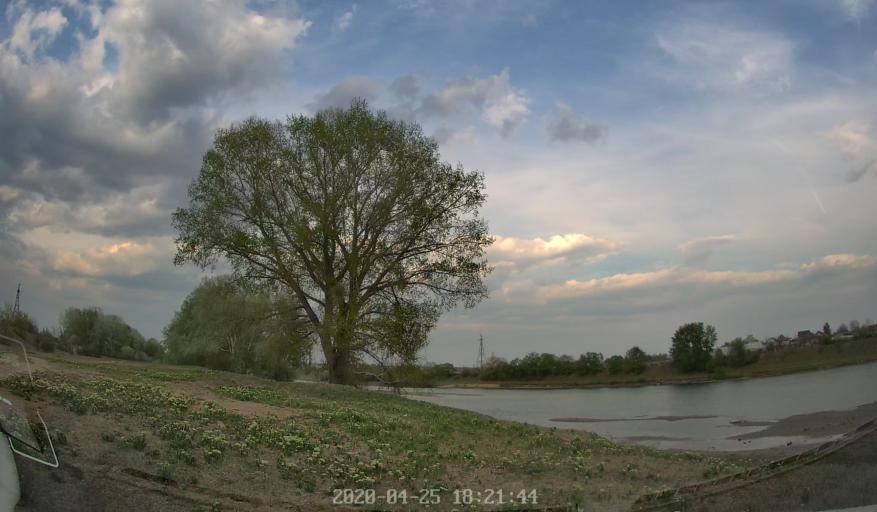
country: MD
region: Criuleni
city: Criuleni
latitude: 47.1557
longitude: 29.1322
